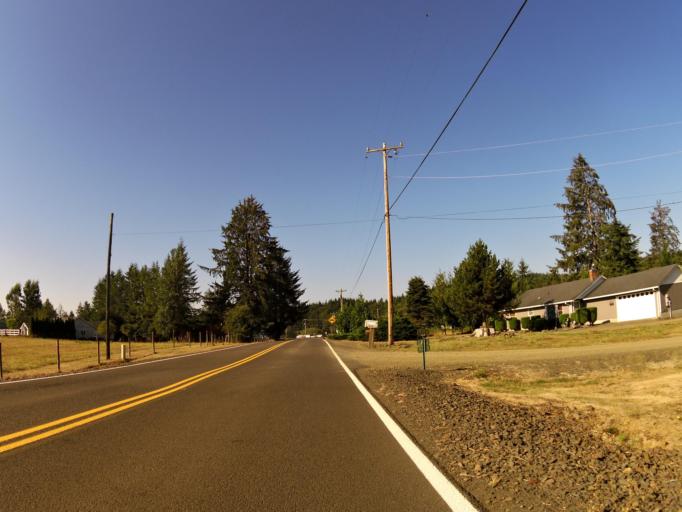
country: US
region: Oregon
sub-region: Tillamook County
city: Tillamook
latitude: 45.3844
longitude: -123.8012
